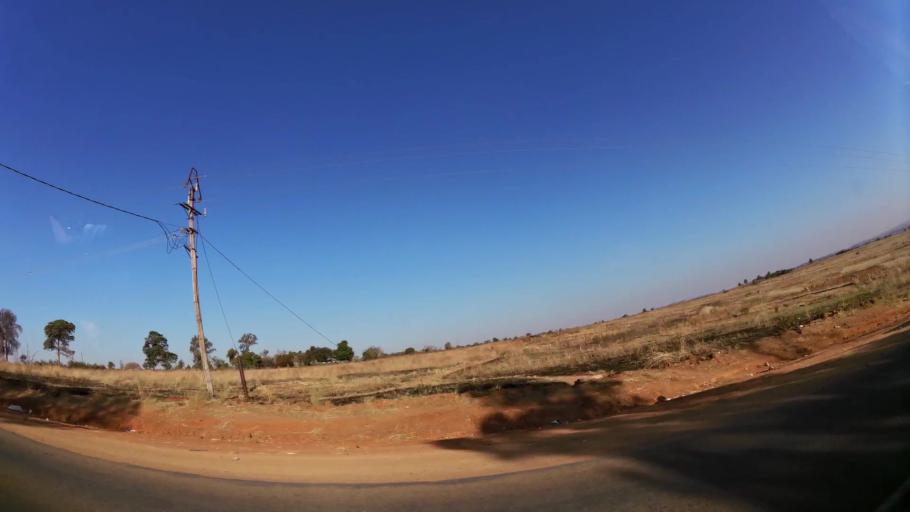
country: ZA
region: Gauteng
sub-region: West Rand District Municipality
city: Muldersdriseloop
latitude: -26.0037
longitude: 27.9182
